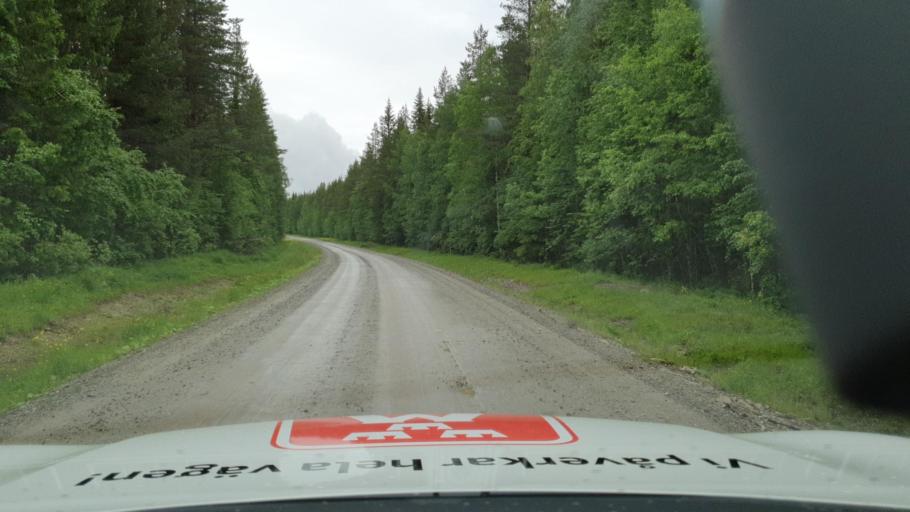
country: SE
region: Vaesterbotten
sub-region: Dorotea Kommun
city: Dorotea
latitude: 64.0772
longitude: 16.6909
